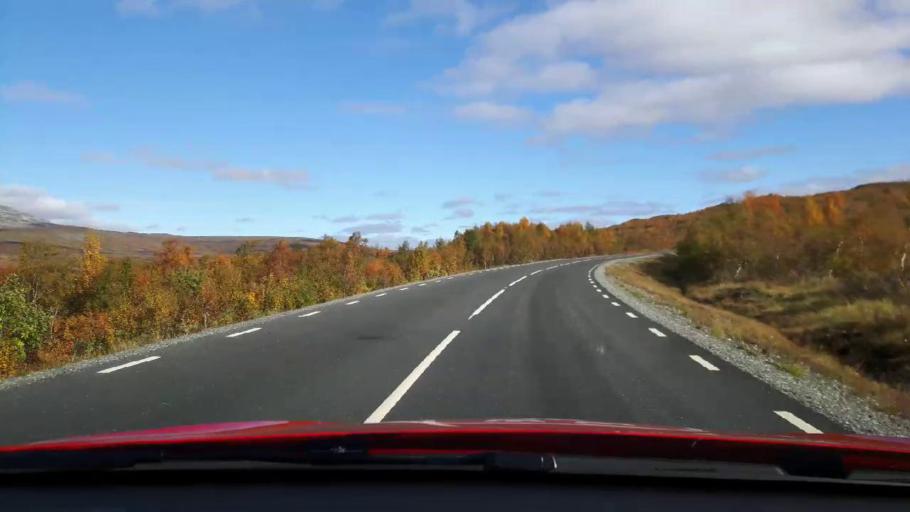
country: NO
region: Nordland
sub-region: Hattfjelldal
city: Hattfjelldal
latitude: 64.9945
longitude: 14.2314
